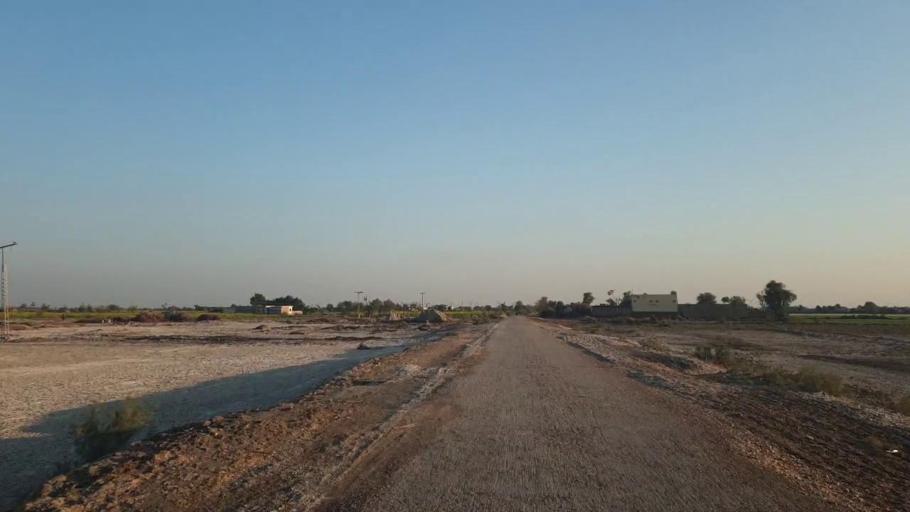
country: PK
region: Sindh
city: Khadro
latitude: 26.0793
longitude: 68.6870
